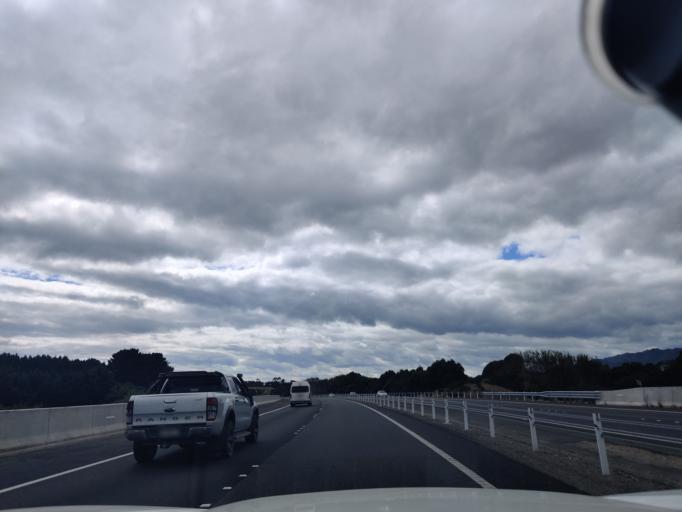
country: NZ
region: Wellington
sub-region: Kapiti Coast District
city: Paraparaumu
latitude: -40.8899
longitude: 175.0232
